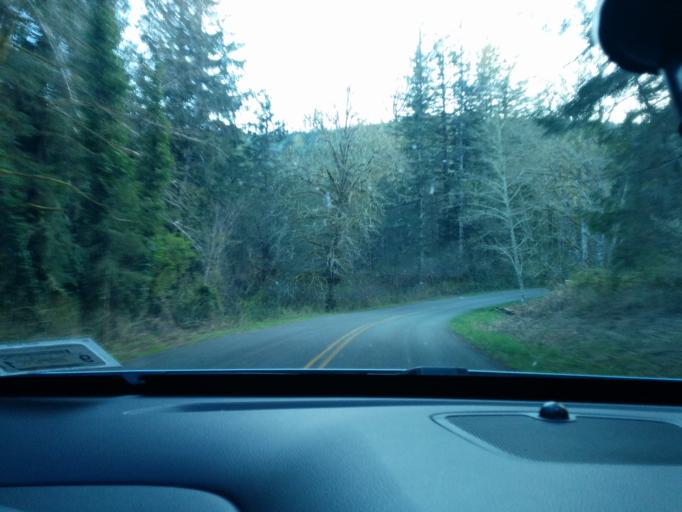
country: US
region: Washington
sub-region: Snohomish County
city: Gold Bar
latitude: 47.8975
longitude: -121.7548
